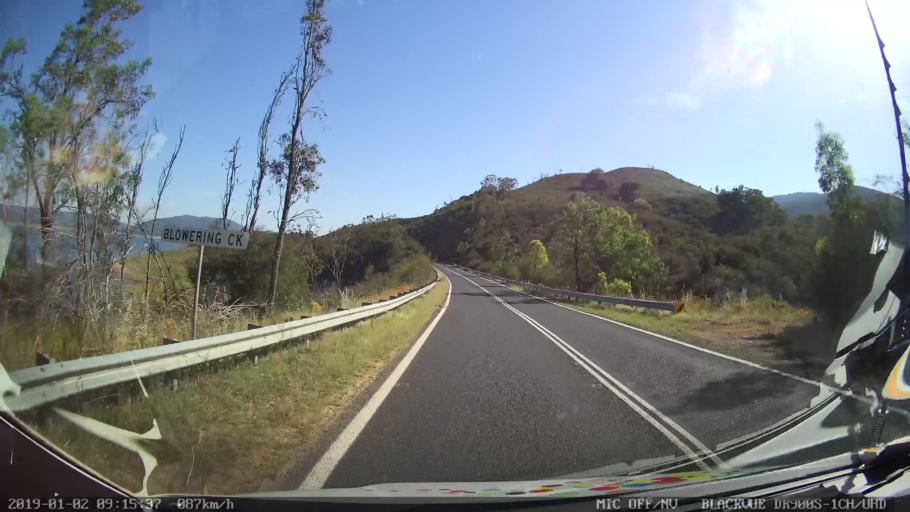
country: AU
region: New South Wales
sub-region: Tumut Shire
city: Tumut
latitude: -35.4630
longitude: 148.2808
